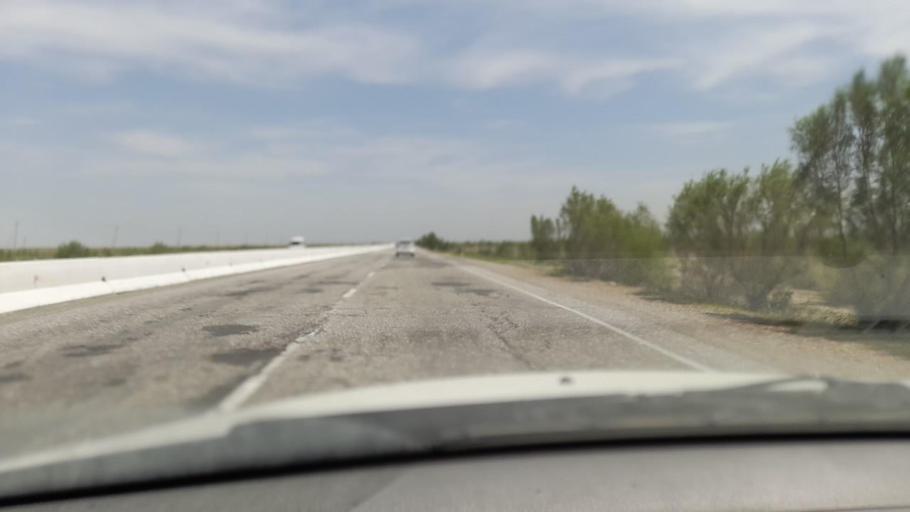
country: UZ
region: Navoiy
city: Qiziltepa
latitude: 40.0965
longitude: 64.9884
